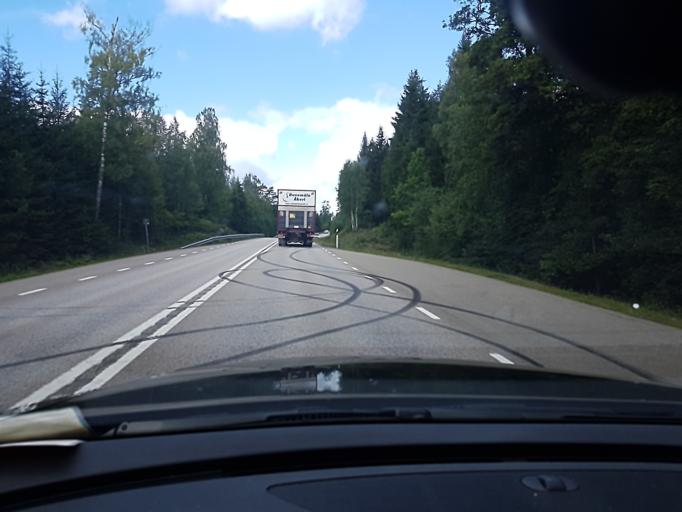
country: SE
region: Kronoberg
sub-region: Lessebo Kommun
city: Lessebo
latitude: 56.7304
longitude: 15.2990
